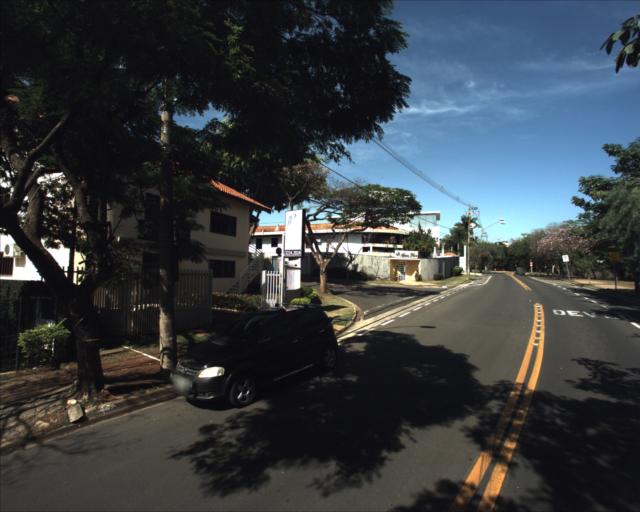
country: BR
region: Sao Paulo
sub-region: Sorocaba
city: Sorocaba
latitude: -23.5258
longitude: -47.4684
